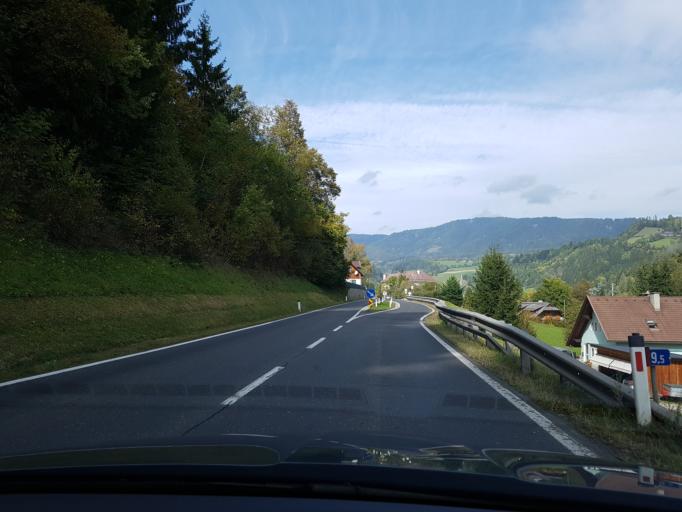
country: AT
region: Carinthia
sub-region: Politischer Bezirk Feldkirchen
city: Himmelberg
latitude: 46.7445
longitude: 14.0406
